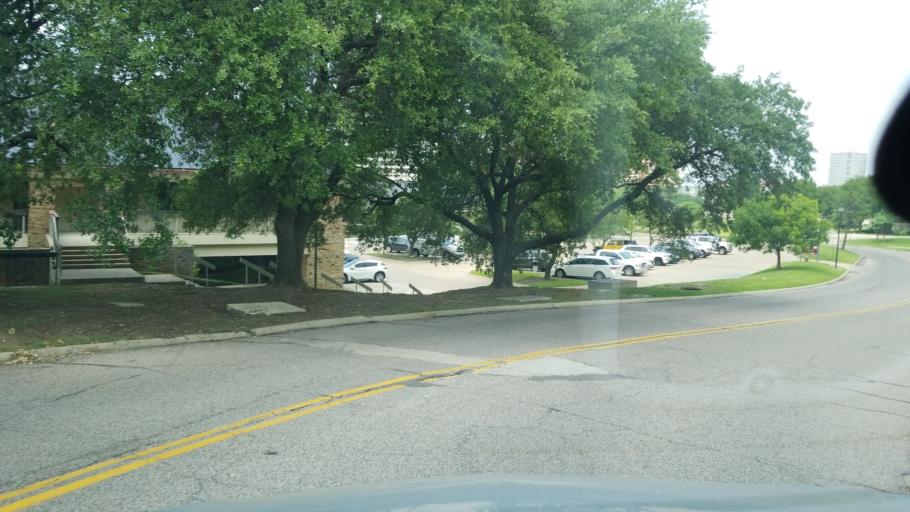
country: US
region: Texas
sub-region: Dallas County
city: Irving
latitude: 32.8590
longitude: -96.9382
